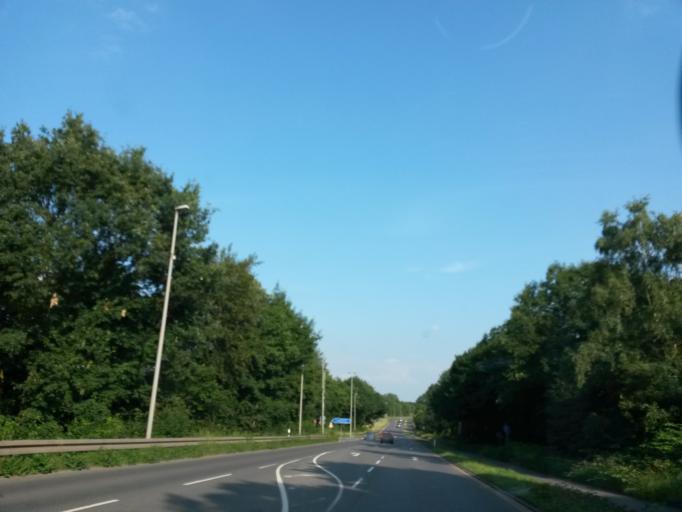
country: DE
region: North Rhine-Westphalia
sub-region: Regierungsbezirk Munster
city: Bottrop
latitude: 51.5383
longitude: 6.8712
